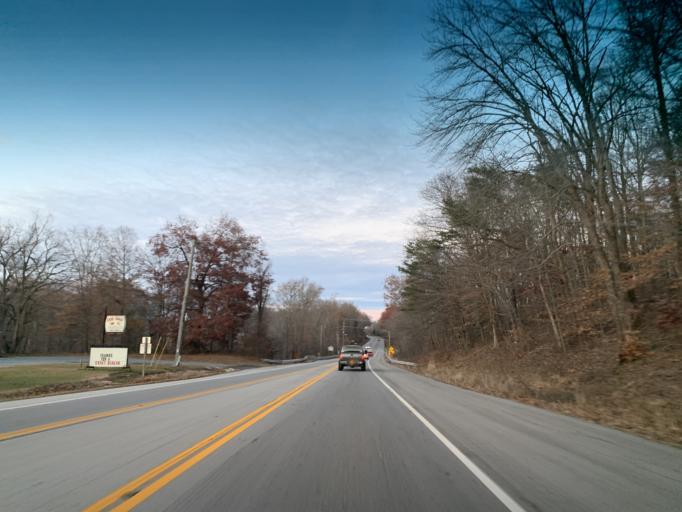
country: US
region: Maryland
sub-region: Cecil County
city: Elkton
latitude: 39.5380
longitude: -75.8083
